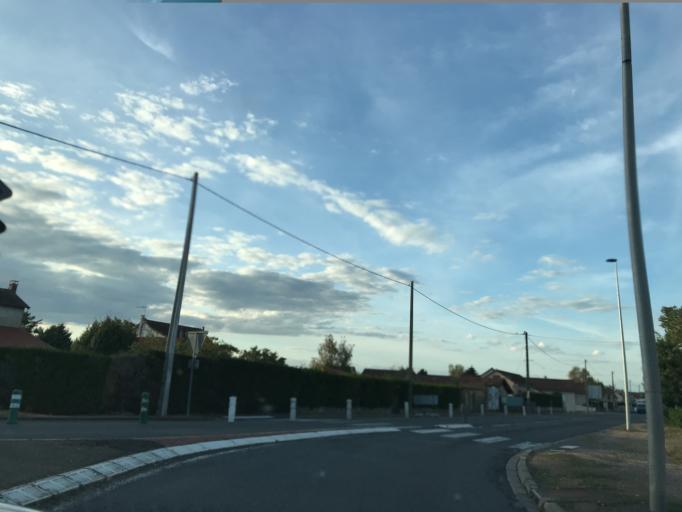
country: FR
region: Auvergne
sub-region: Departement de l'Allier
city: Saint-Yorre
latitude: 46.0543
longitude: 3.4691
